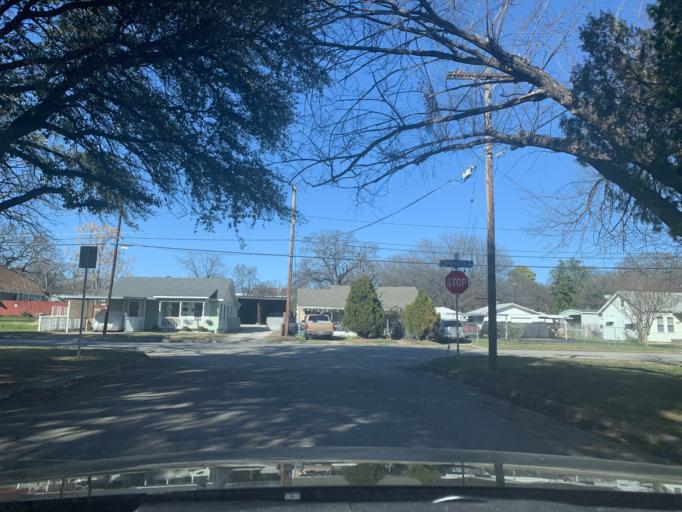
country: US
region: Texas
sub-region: Tarrant County
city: Haltom City
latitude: 32.7814
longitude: -97.2819
